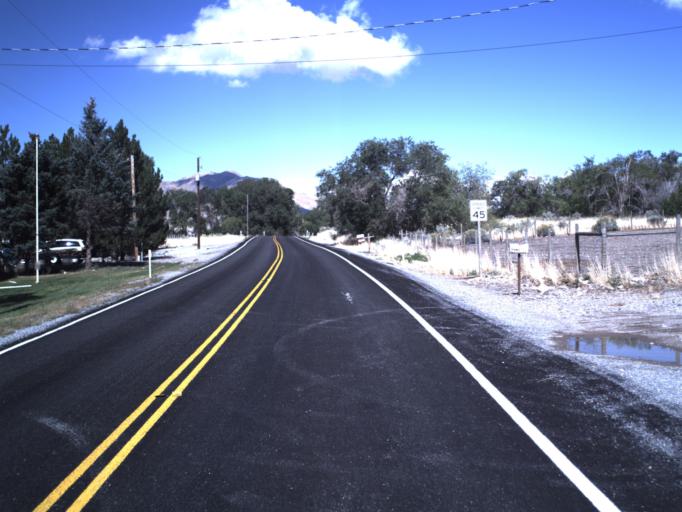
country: US
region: Utah
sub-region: Utah County
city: Genola
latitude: 39.9741
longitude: -111.8499
